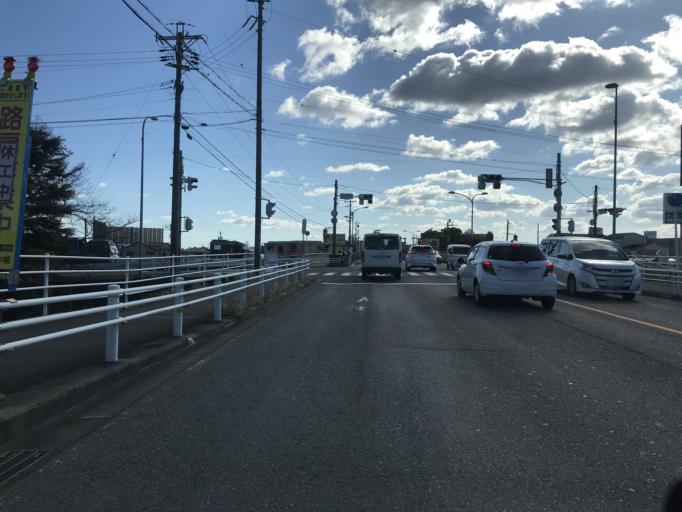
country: JP
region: Aichi
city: Nagoya-shi
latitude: 35.2061
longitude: 136.8575
